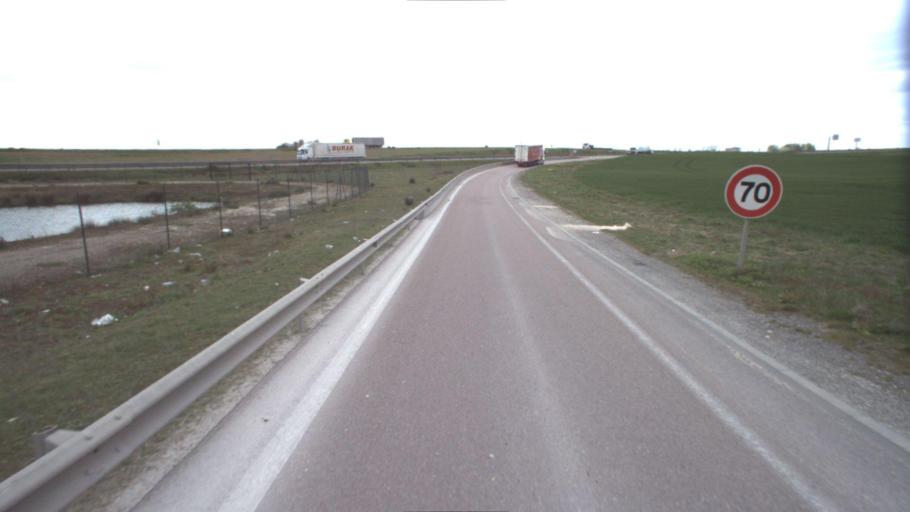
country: FR
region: Ile-de-France
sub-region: Departement de Seine-et-Marne
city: Jouy-le-Chatel
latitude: 48.6858
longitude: 3.1026
